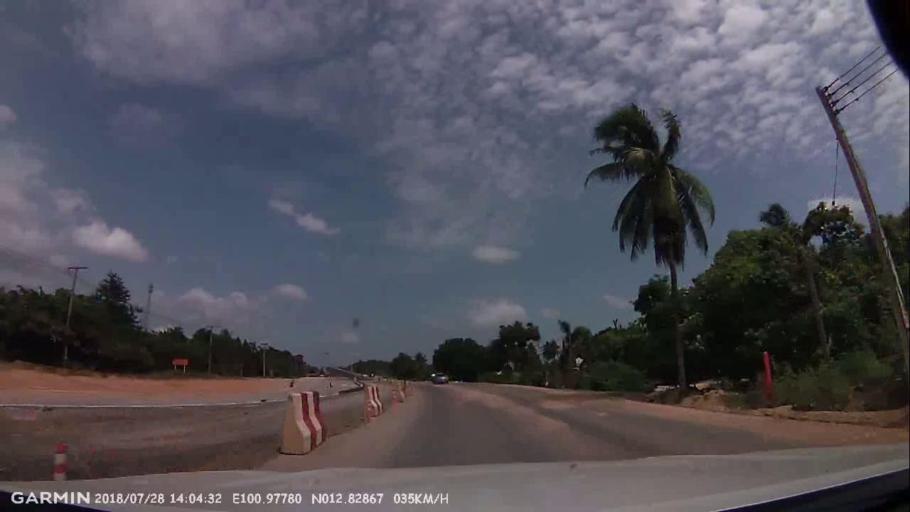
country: TH
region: Rayong
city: Ban Chang
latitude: 12.8285
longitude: 100.9778
